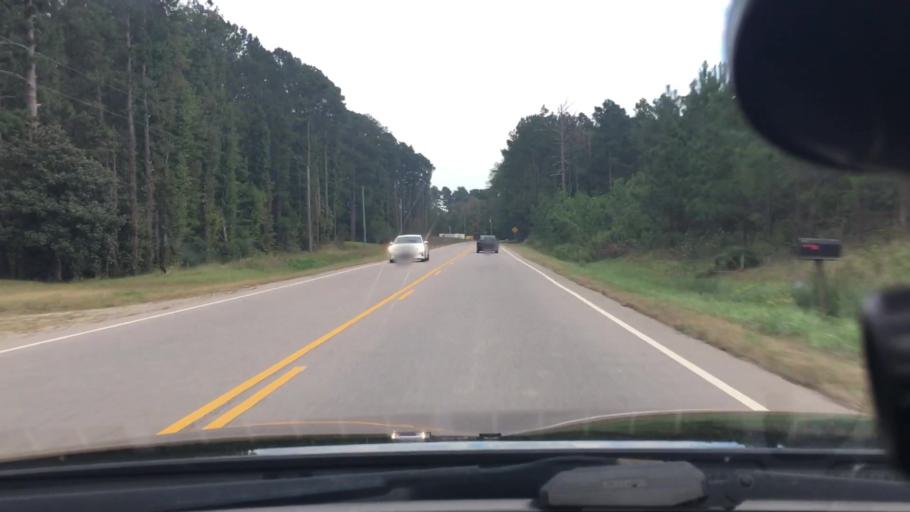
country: US
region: North Carolina
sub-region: Moore County
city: Carthage
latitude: 35.3810
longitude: -79.4796
